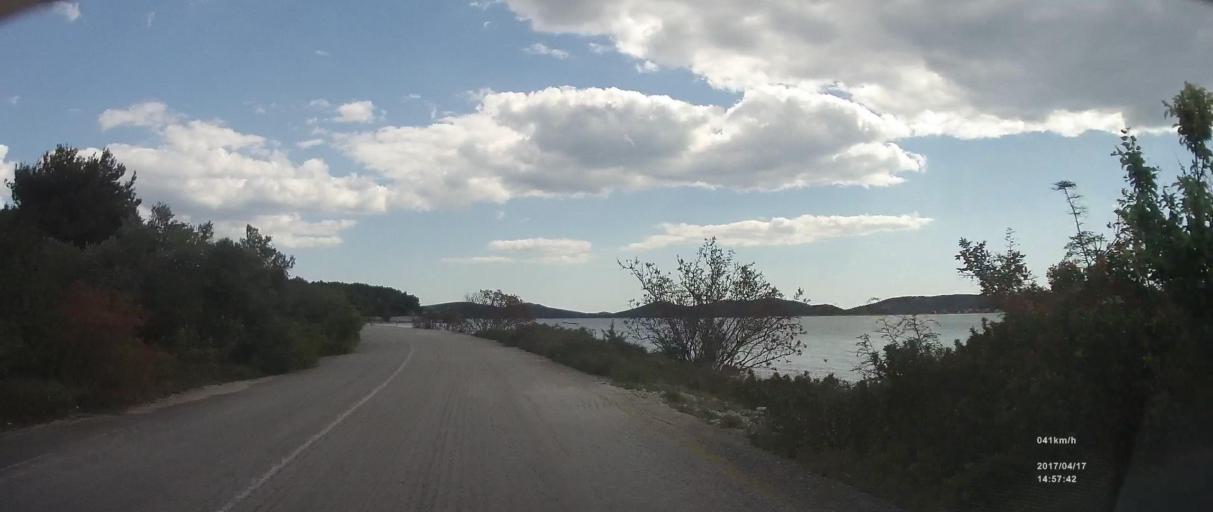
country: HR
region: Sibensko-Kniniska
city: Murter
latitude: 43.8424
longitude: 15.6258
